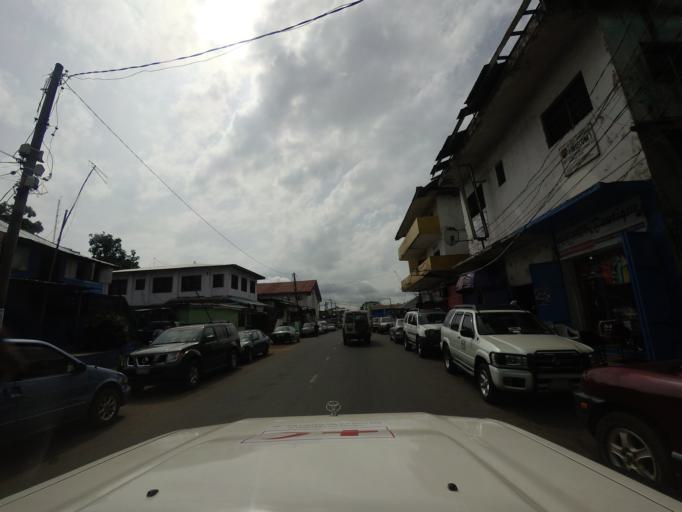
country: LR
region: Montserrado
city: Monrovia
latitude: 6.3156
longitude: -10.8048
